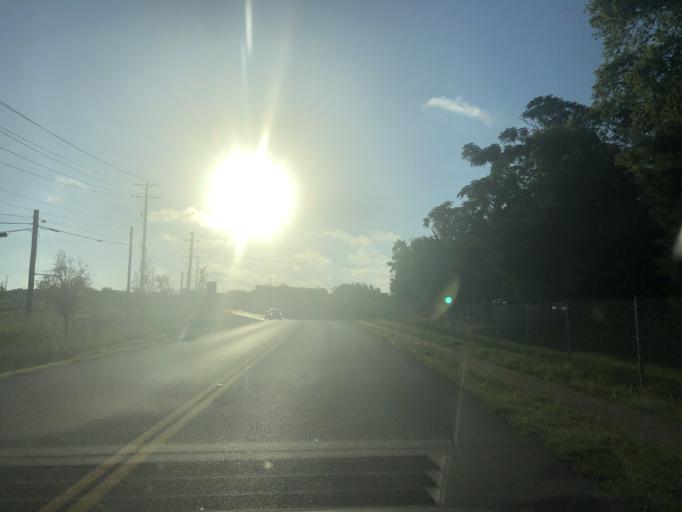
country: US
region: Texas
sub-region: Dallas County
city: Duncanville
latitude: 32.6619
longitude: -96.9654
